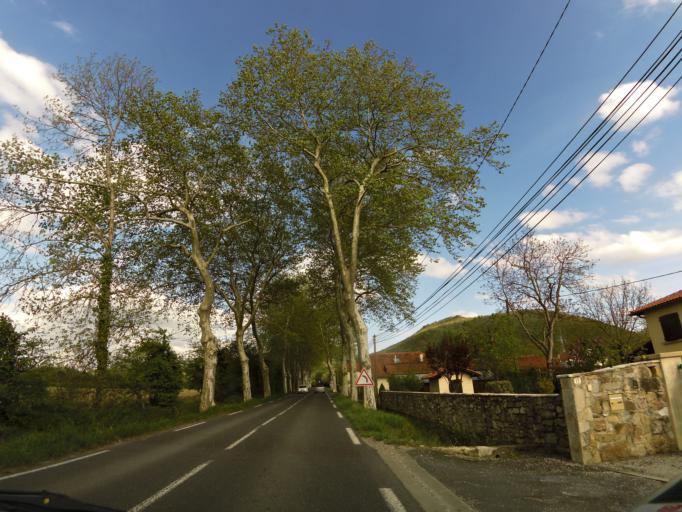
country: FR
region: Midi-Pyrenees
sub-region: Departement du Tarn
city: Soreze
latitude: 43.4504
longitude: 2.0582
